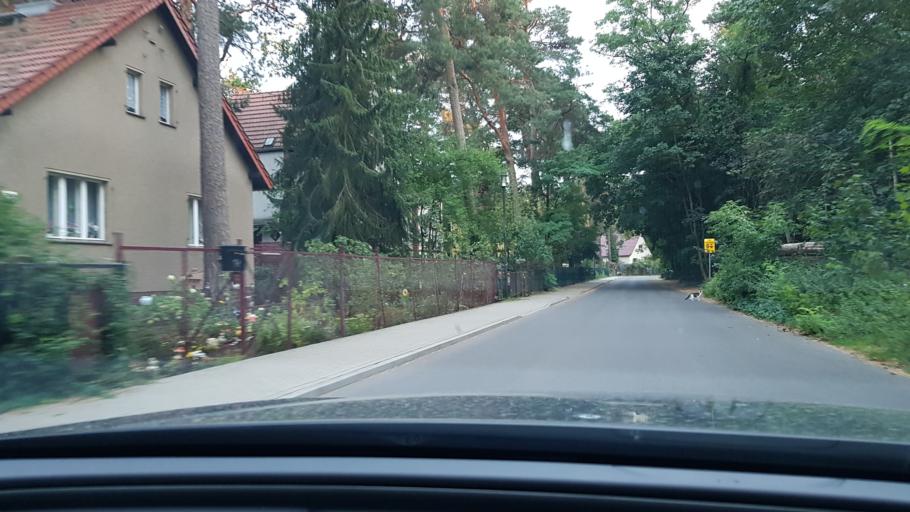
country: DE
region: Berlin
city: Friedrichshagen
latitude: 52.4816
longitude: 13.6284
